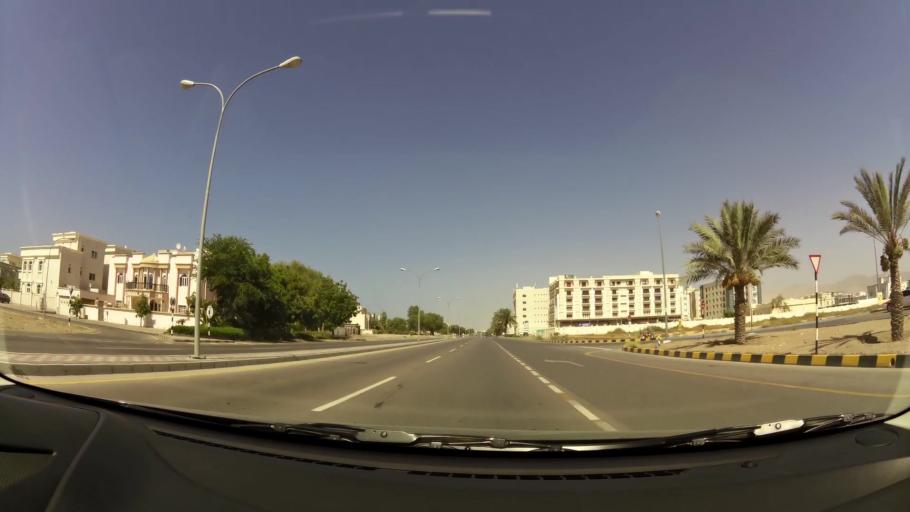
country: OM
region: Muhafazat Masqat
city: Bawshar
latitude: 23.6022
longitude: 58.3557
